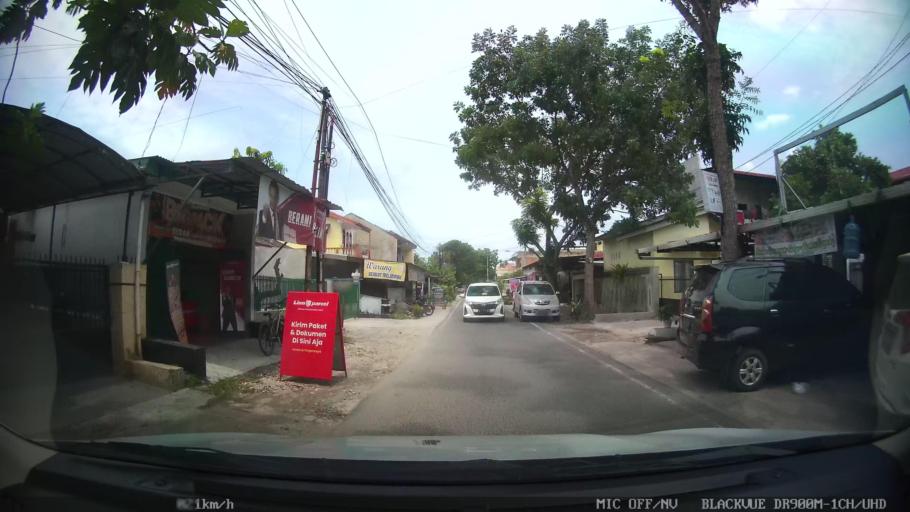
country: ID
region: North Sumatra
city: Medan
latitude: 3.5551
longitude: 98.6589
